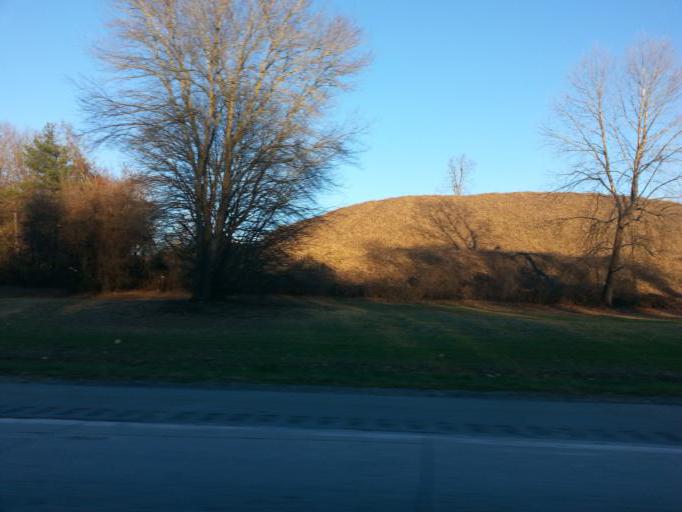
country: US
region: North Carolina
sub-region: Henderson County
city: Fletcher
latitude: 35.4231
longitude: -82.5275
